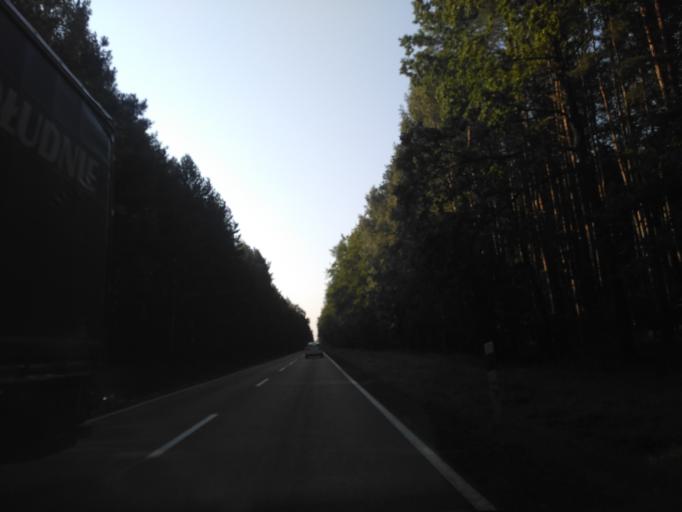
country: PL
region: Subcarpathian Voivodeship
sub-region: Powiat nizanski
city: Nisko
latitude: 50.4919
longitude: 22.1395
